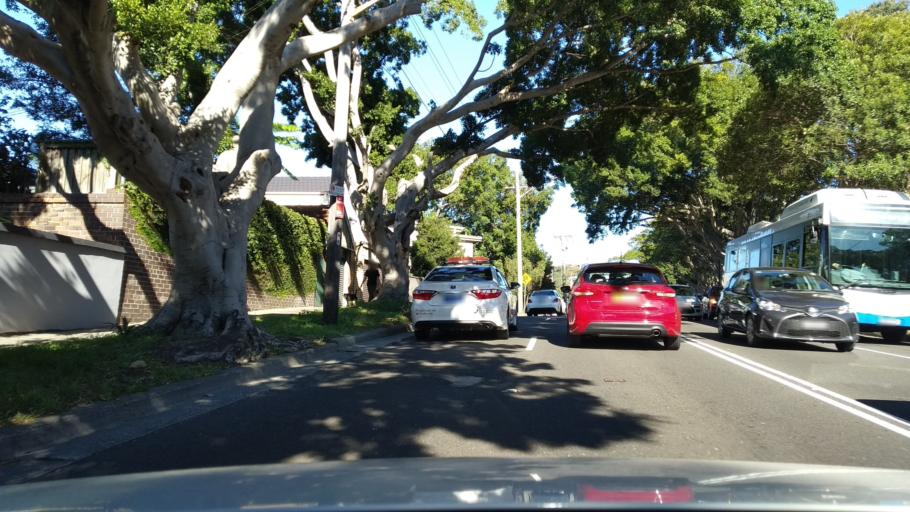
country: AU
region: New South Wales
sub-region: Waverley
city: Bondi Beach
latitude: -33.8866
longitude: 151.2664
